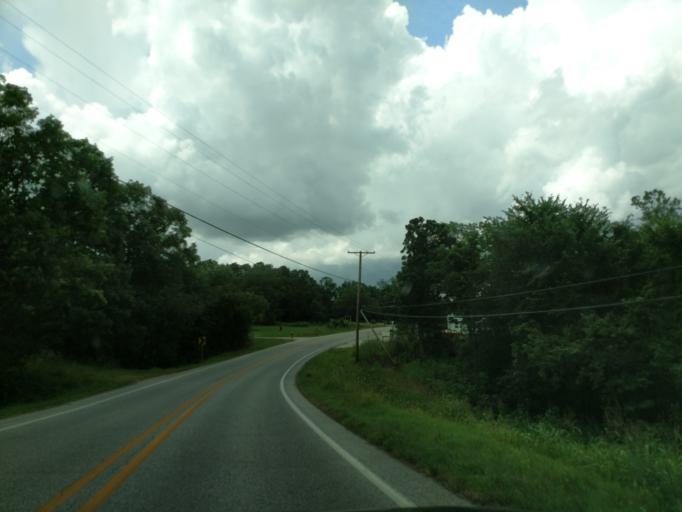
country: US
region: Arkansas
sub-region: Boone County
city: Harrison
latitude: 36.2425
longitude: -93.2120
